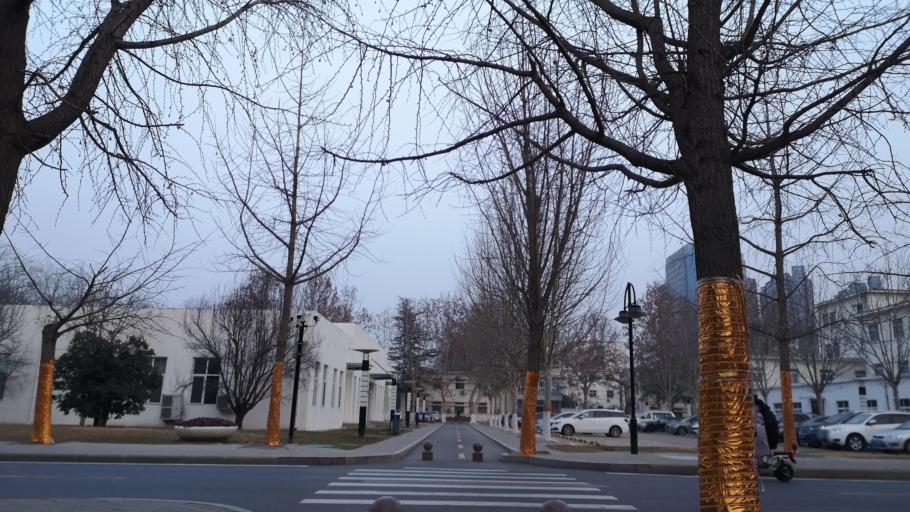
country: CN
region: Henan Sheng
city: Zhongyuanlu
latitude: 35.7768
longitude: 115.0752
